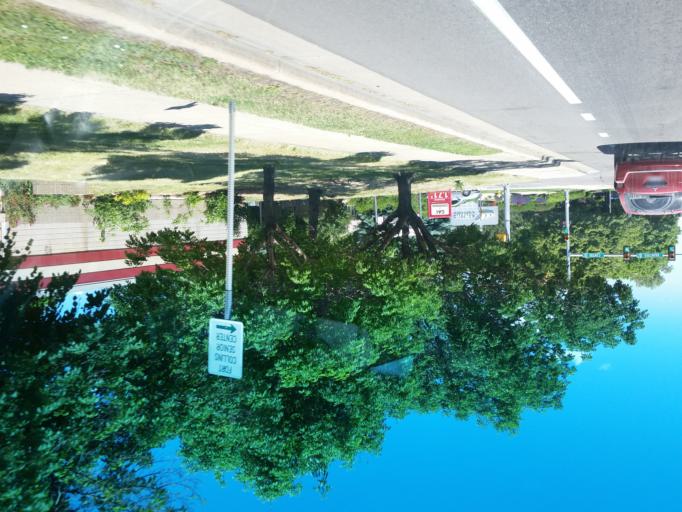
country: US
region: Colorado
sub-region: Larimer County
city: Fort Collins
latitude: 40.5550
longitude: -105.0960
